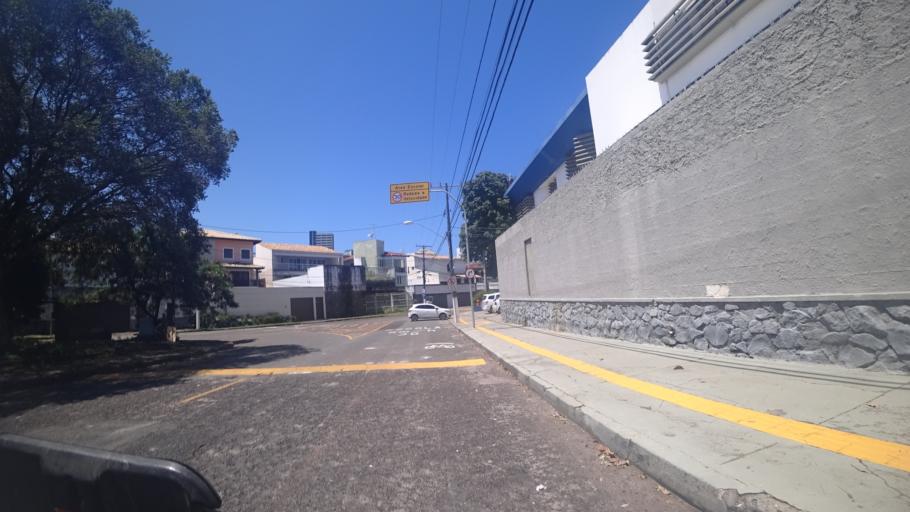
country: BR
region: Bahia
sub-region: Salvador
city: Salvador
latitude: -12.9916
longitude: -38.4698
